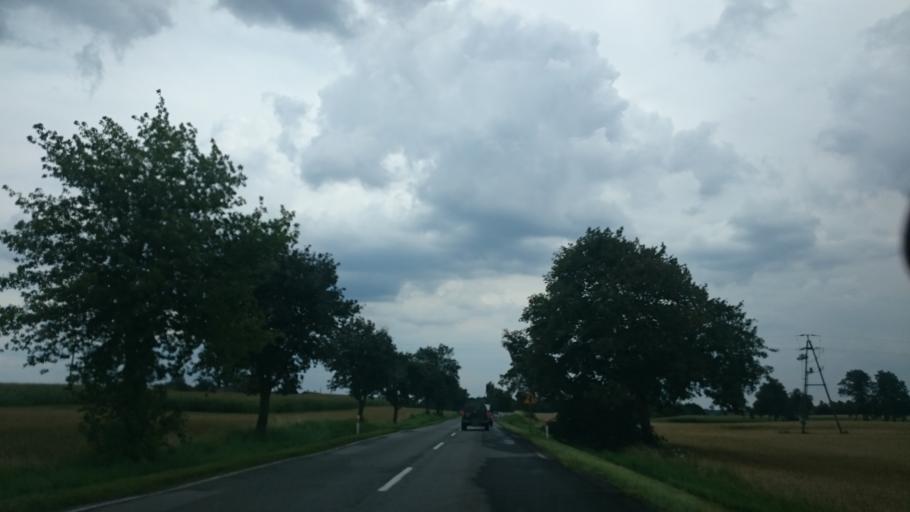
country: PL
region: Kujawsko-Pomorskie
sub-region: Powiat tucholski
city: Cekcyn
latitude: 53.5124
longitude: 17.9717
